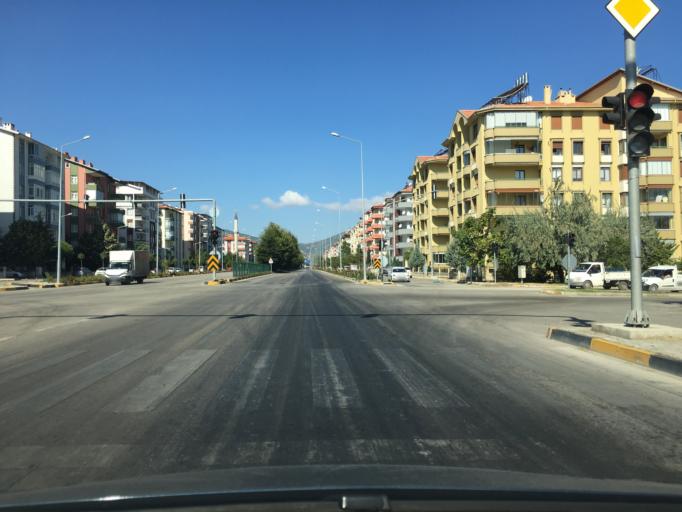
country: TR
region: Isparta
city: Isparta
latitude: 37.7883
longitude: 30.5551
